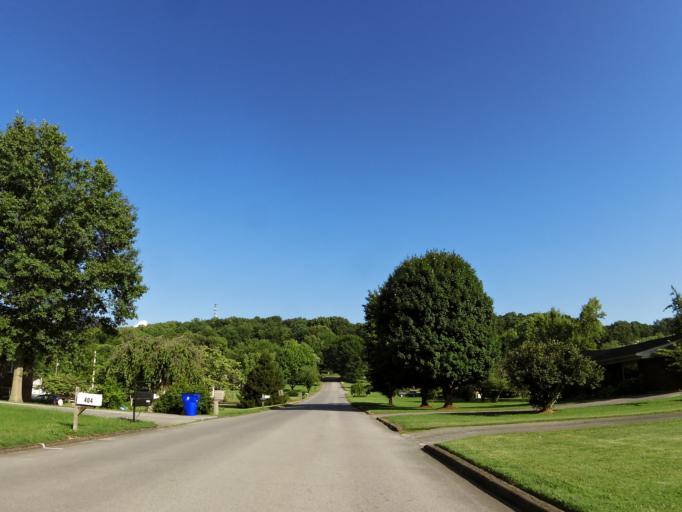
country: US
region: Tennessee
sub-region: Blount County
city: Eagleton Village
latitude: 35.7970
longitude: -83.9341
